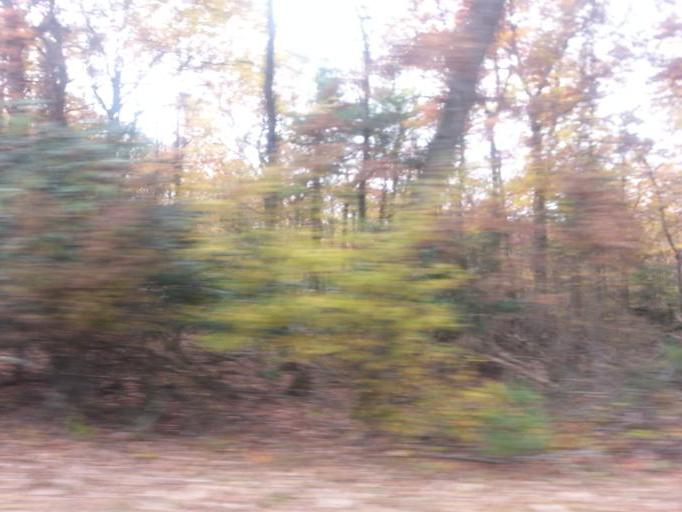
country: US
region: Virginia
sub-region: City of Galax
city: Galax
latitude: 36.5439
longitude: -80.9181
